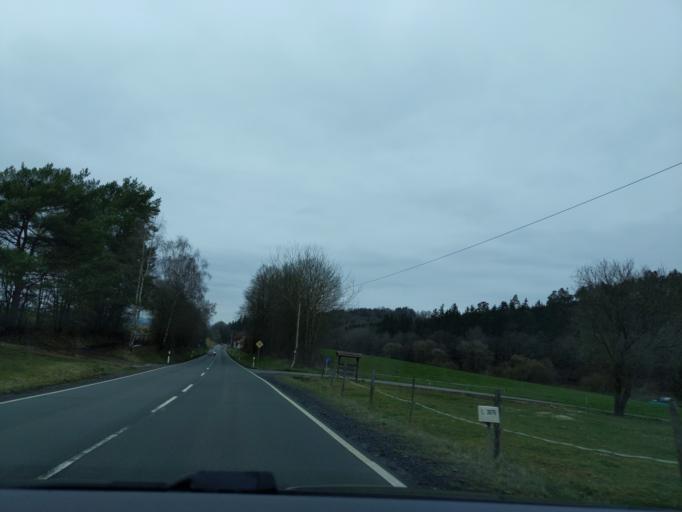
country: DE
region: Hesse
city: Frankenberg
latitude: 51.0239
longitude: 8.8246
